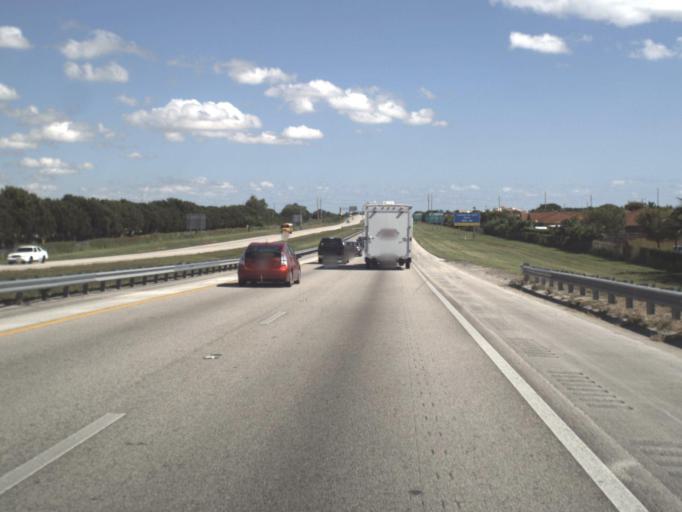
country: US
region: Florida
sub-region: Miami-Dade County
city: Homestead
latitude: 25.4636
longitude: -80.4604
